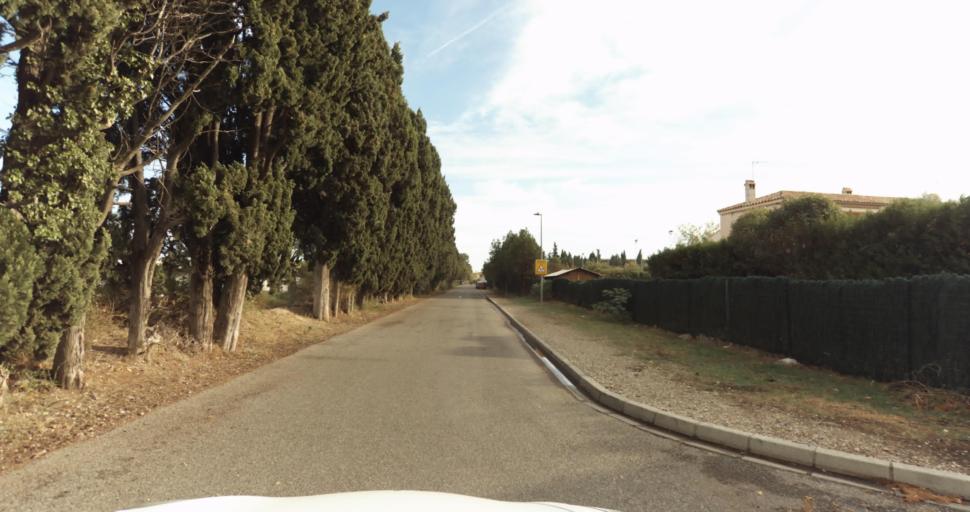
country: FR
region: Provence-Alpes-Cote d'Azur
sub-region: Departement des Bouches-du-Rhone
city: Miramas
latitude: 43.5861
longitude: 4.9966
